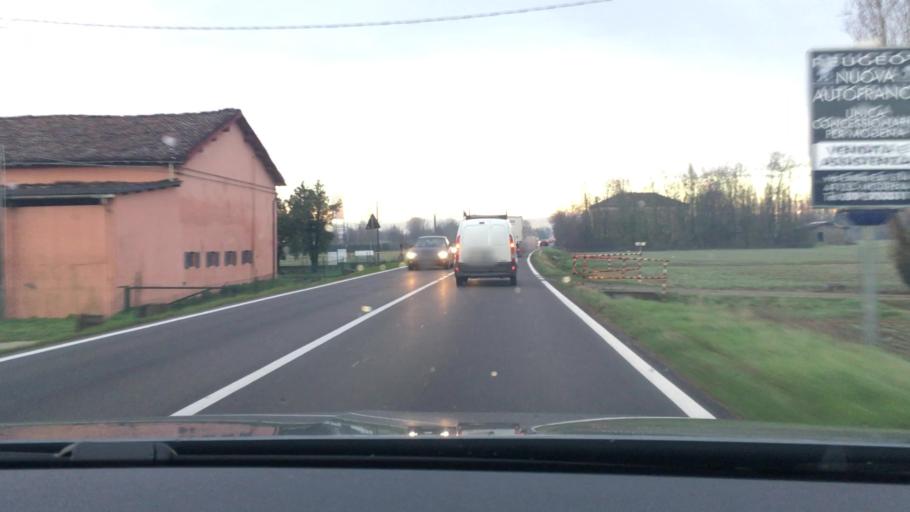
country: IT
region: Emilia-Romagna
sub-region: Provincia di Modena
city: Albareto
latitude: 44.6899
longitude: 10.9427
